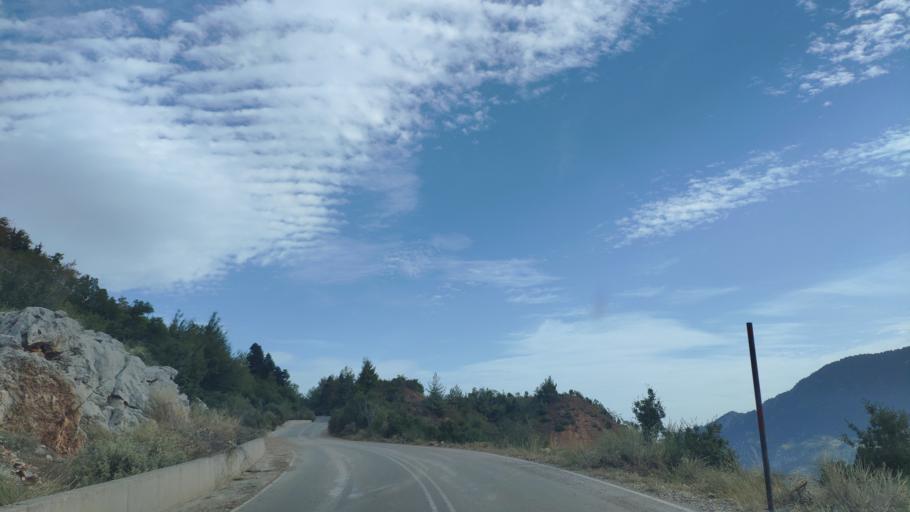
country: GR
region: Central Greece
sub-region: Nomos Fokidos
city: Amfissa
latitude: 38.6413
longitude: 22.3842
